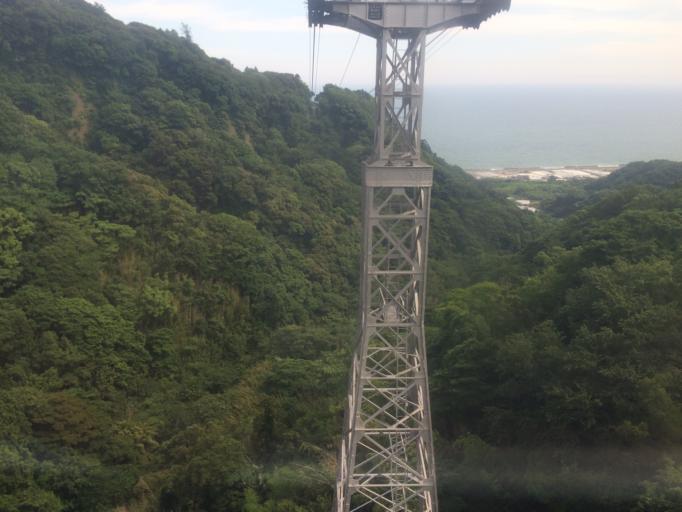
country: JP
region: Shizuoka
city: Shizuoka-shi
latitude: 34.9684
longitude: 138.4655
